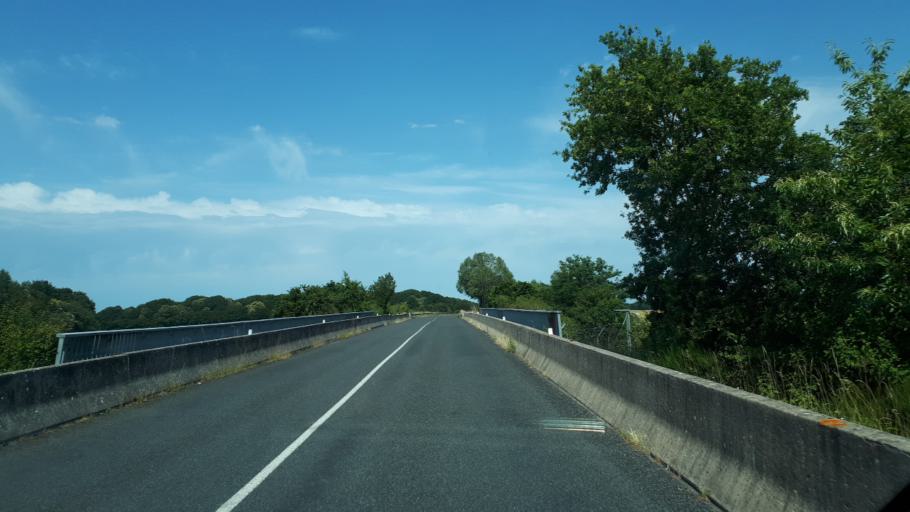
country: FR
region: Centre
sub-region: Departement du Loir-et-Cher
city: La Ville-aux-Clercs
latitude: 47.9687
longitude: 1.0522
